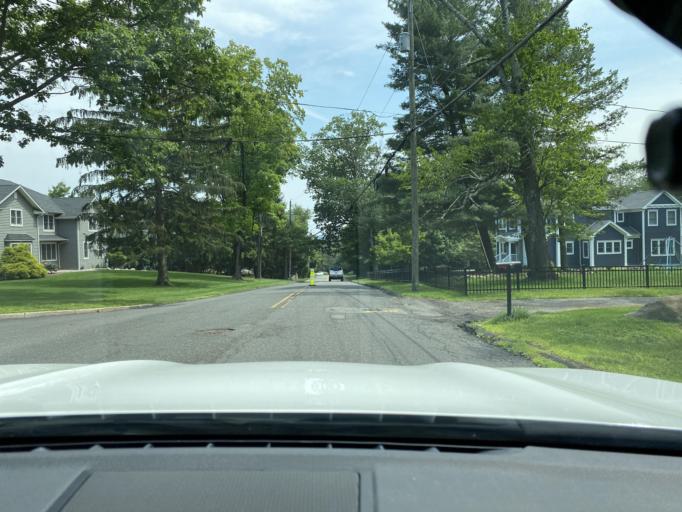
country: US
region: New Jersey
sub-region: Bergen County
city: Upper Saddle River
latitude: 41.0790
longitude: -74.1080
